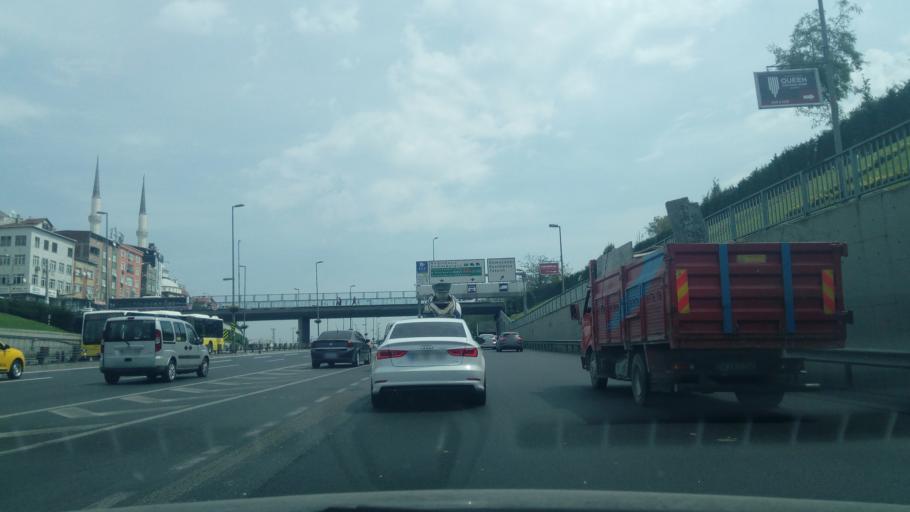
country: TR
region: Istanbul
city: Sisli
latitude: 41.0550
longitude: 28.9570
